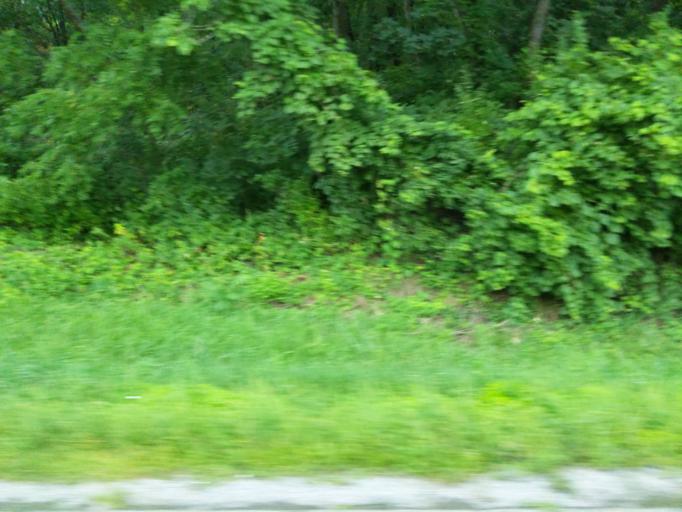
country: US
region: Wisconsin
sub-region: Dane County
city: Mazomanie
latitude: 43.2106
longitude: -89.7514
